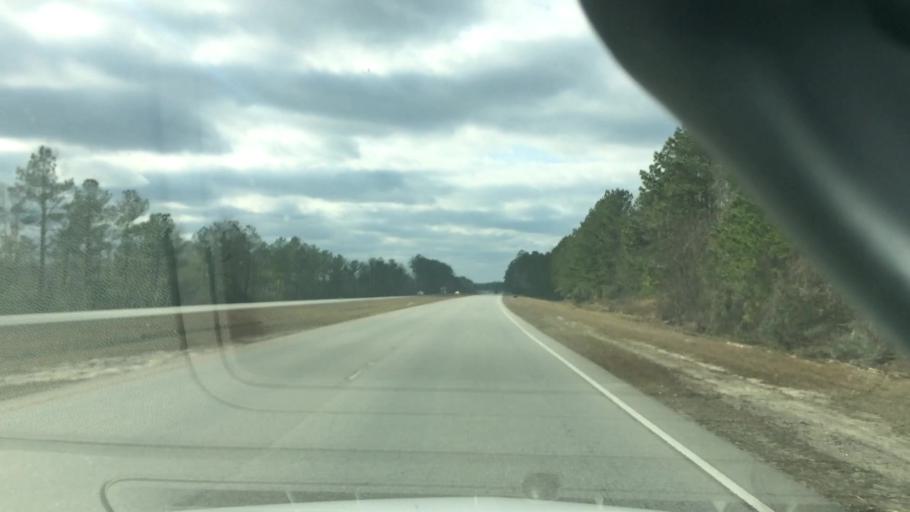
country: US
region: North Carolina
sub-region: Brunswick County
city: Bolivia
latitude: 34.0673
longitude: -78.1816
